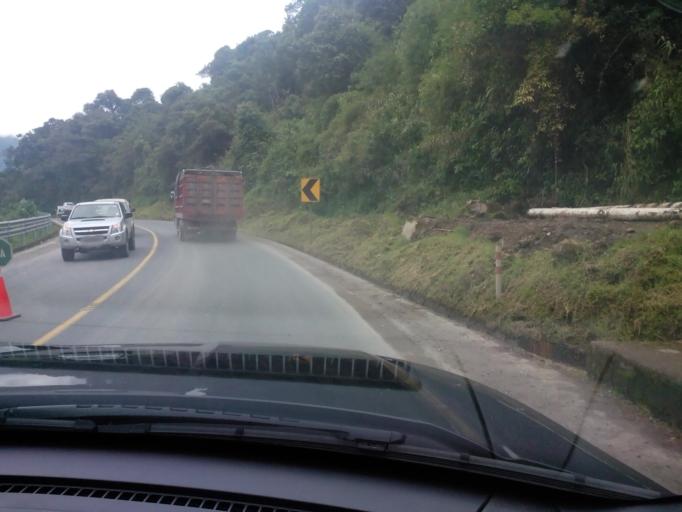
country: EC
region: Pichincha
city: Sangolqui
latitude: -0.4173
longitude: -78.0158
